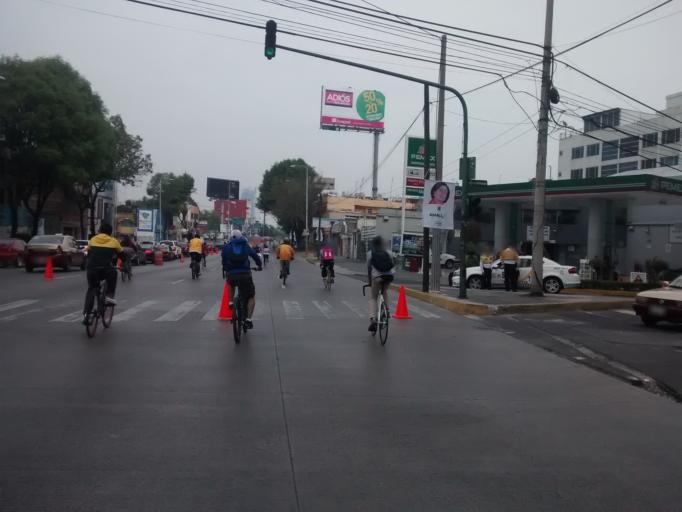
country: MX
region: Mexico City
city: Colonia del Valle
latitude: 19.3971
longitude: -99.1809
